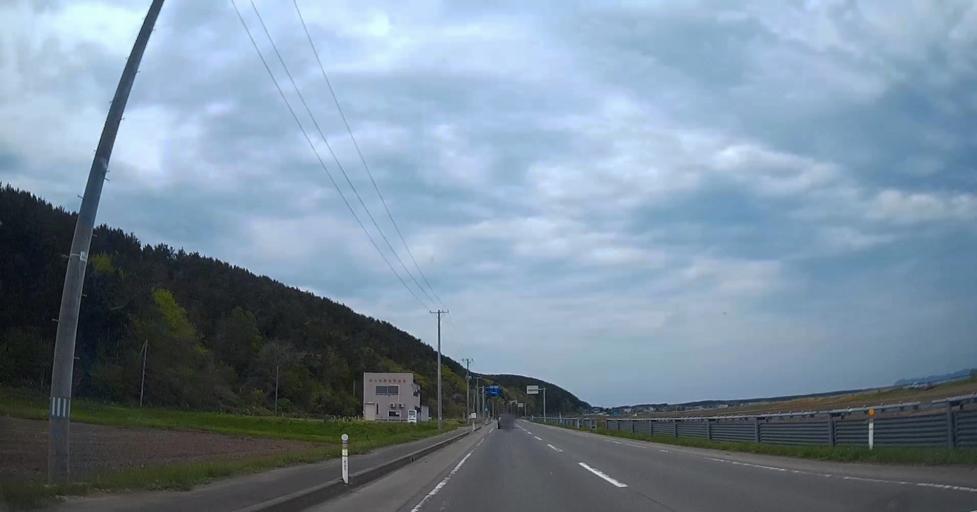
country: JP
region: Aomori
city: Shimokizukuri
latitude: 40.9945
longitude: 140.3554
